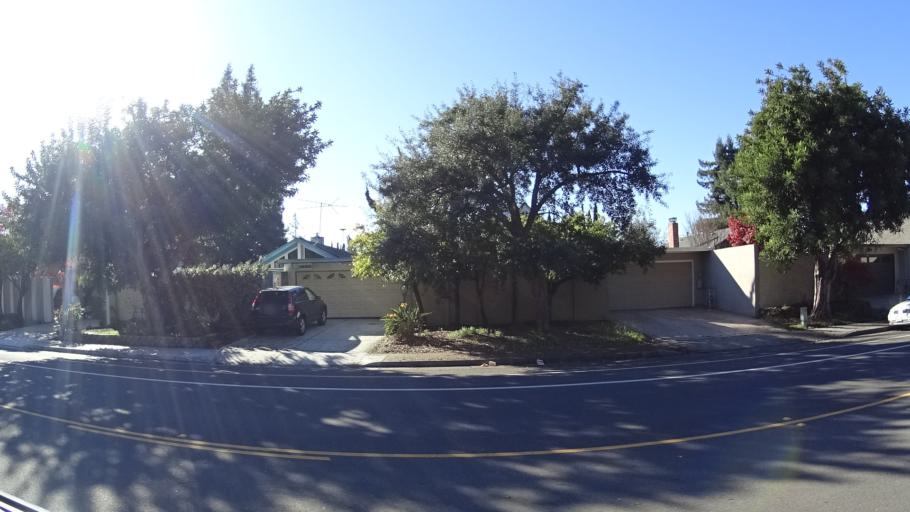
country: US
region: California
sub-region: Santa Clara County
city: Sunnyvale
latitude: 37.3681
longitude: -122.0038
